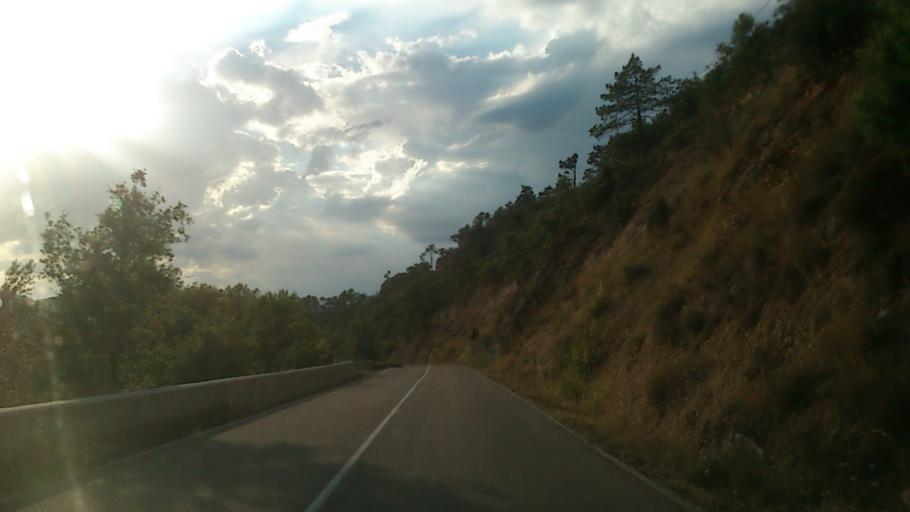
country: ES
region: Castille and Leon
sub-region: Provincia de Burgos
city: Trespaderne
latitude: 42.7915
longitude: -3.3408
